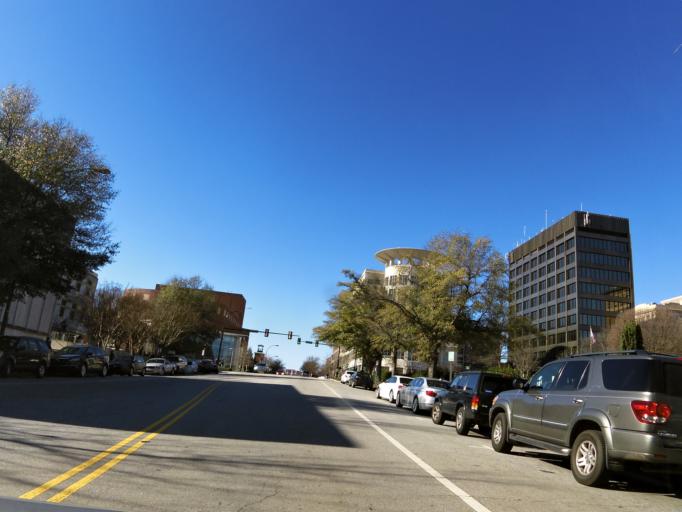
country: US
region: South Carolina
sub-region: Greenville County
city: Greenville
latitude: 34.8473
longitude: -82.3995
